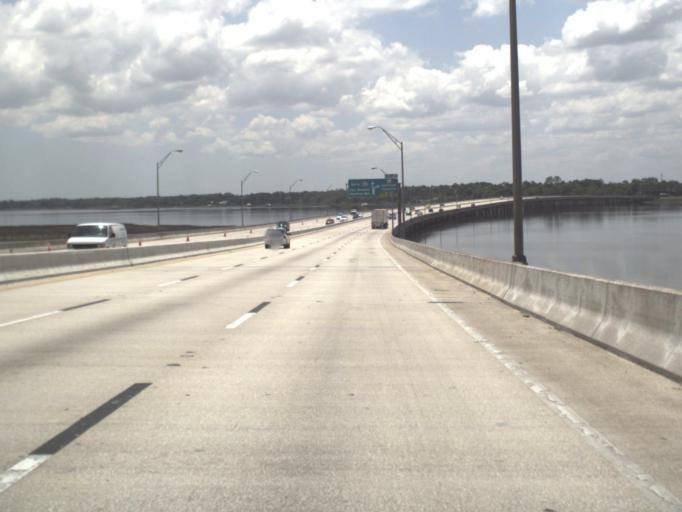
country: US
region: Florida
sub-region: Duval County
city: Jacksonville
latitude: 30.3756
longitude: -81.5532
